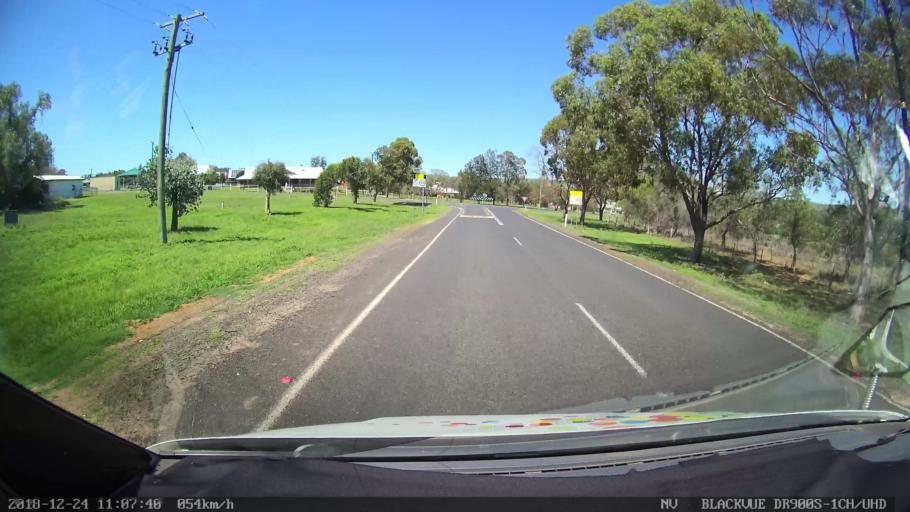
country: AU
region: New South Wales
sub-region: Upper Hunter Shire
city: Merriwa
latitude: -32.1346
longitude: 150.3584
